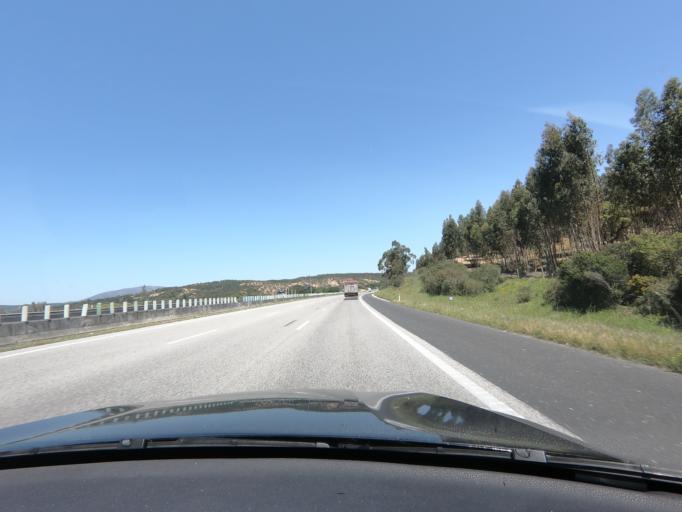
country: PT
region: Lisbon
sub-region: Azambuja
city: Aveiras de Cima
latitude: 39.0960
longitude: -8.9328
